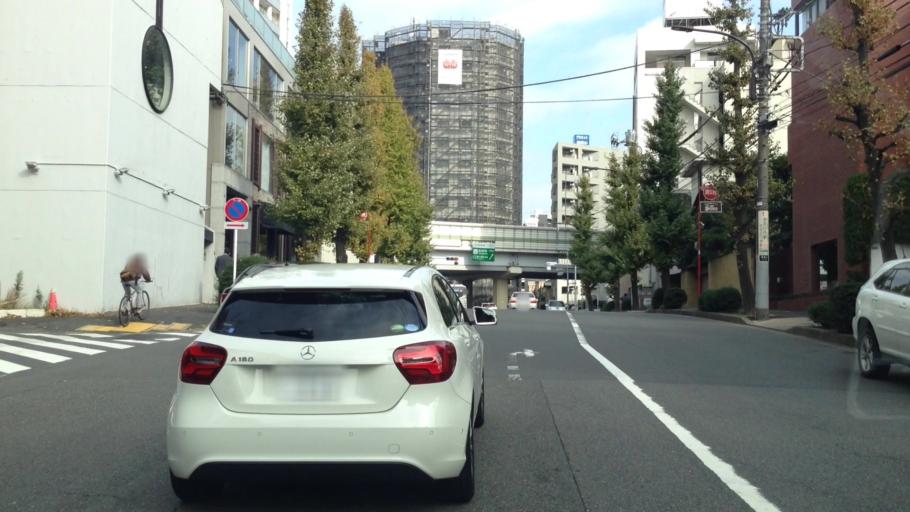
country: JP
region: Tokyo
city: Tokyo
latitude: 35.6580
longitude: 139.7150
